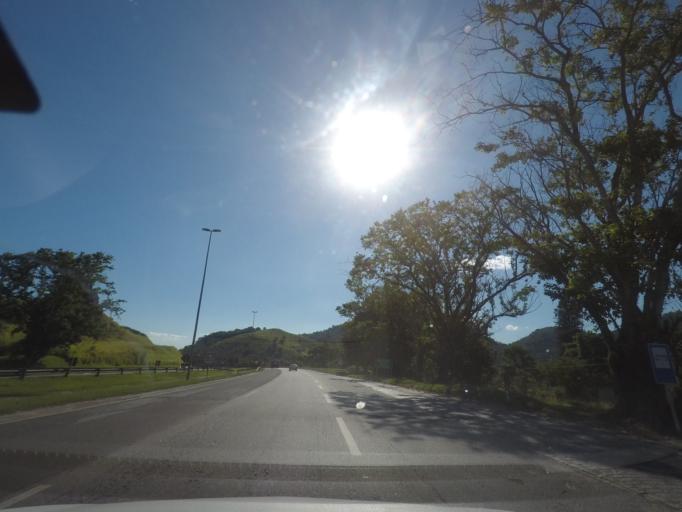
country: BR
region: Rio de Janeiro
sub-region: Guapimirim
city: Guapimirim
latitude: -22.6541
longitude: -43.0850
